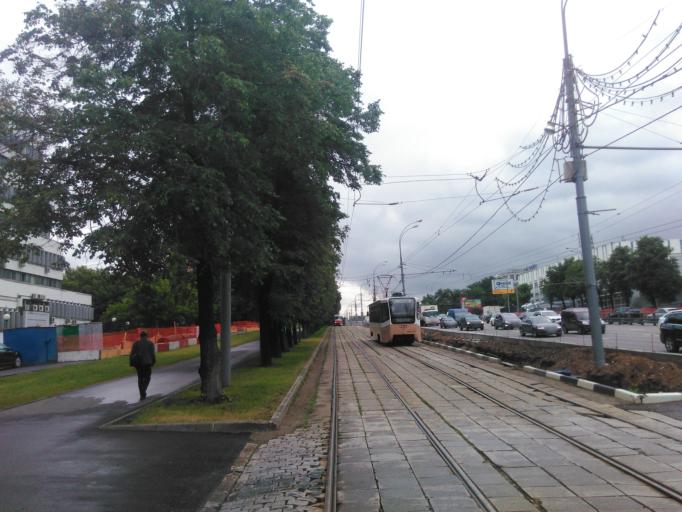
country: RU
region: Moscow
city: Kotlovka
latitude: 55.6884
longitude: 37.6227
